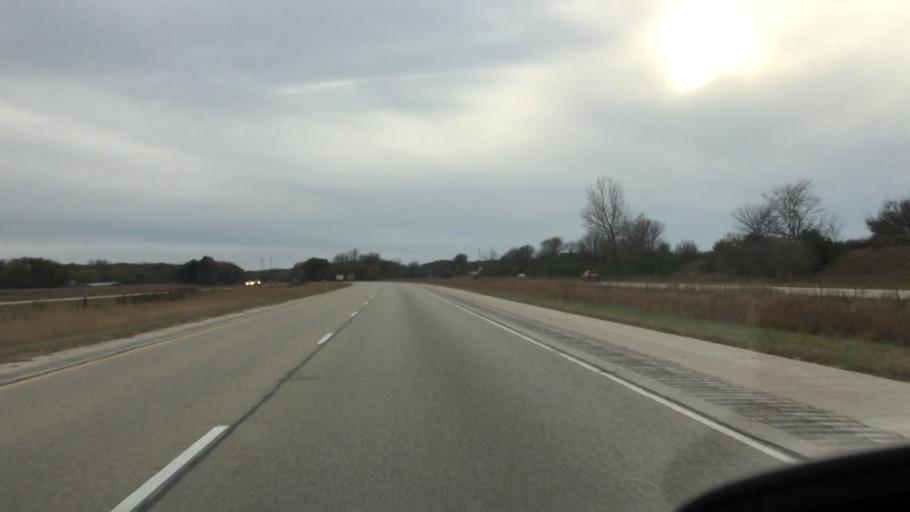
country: US
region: Illinois
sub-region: McLean County
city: Twin Grove
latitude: 40.3819
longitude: -89.0904
